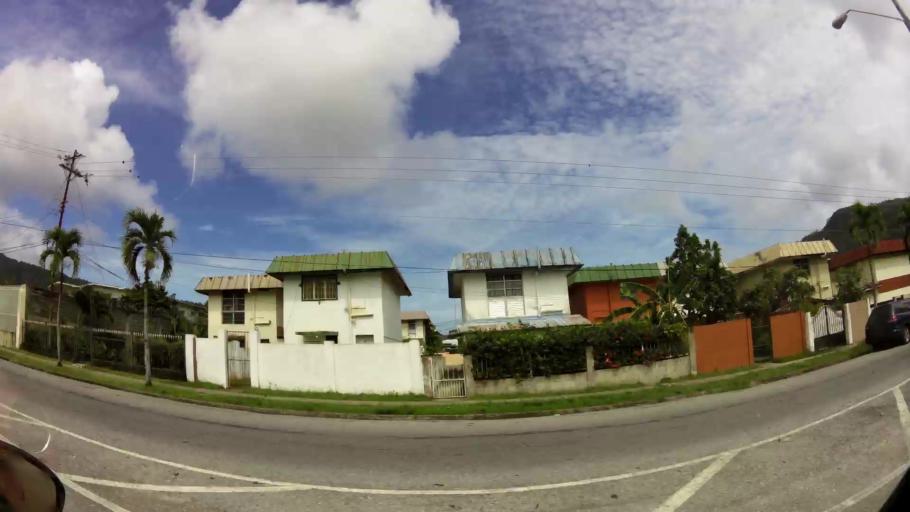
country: TT
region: Diego Martin
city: Petit Valley
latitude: 10.7182
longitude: -61.5610
